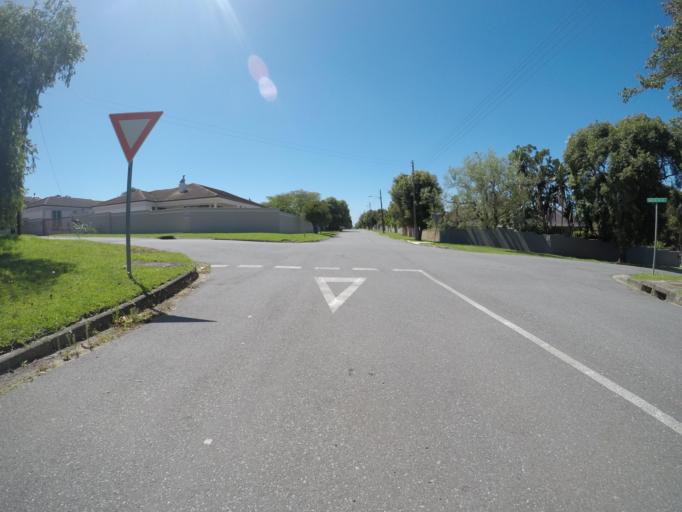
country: ZA
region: Eastern Cape
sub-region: Buffalo City Metropolitan Municipality
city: East London
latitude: -32.9687
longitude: 27.9466
